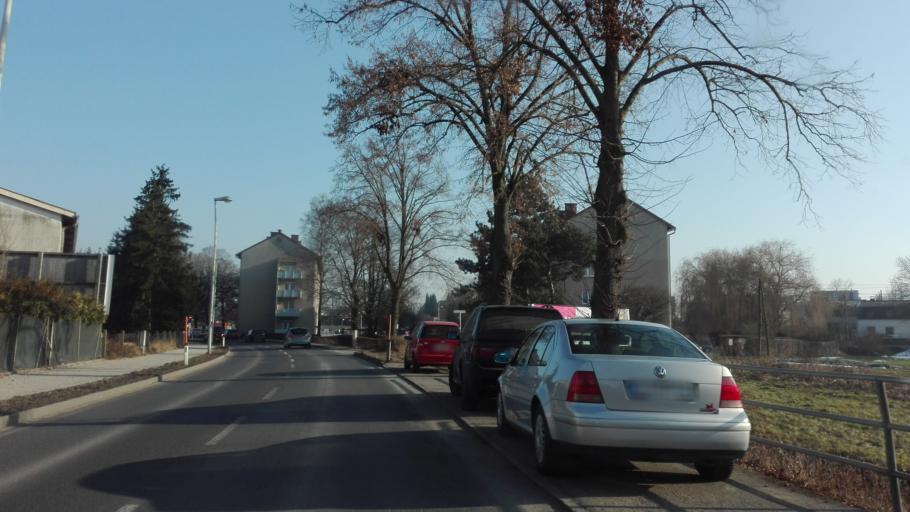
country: AT
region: Upper Austria
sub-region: Politischer Bezirk Linz-Land
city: Leonding
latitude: 48.2758
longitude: 14.2516
